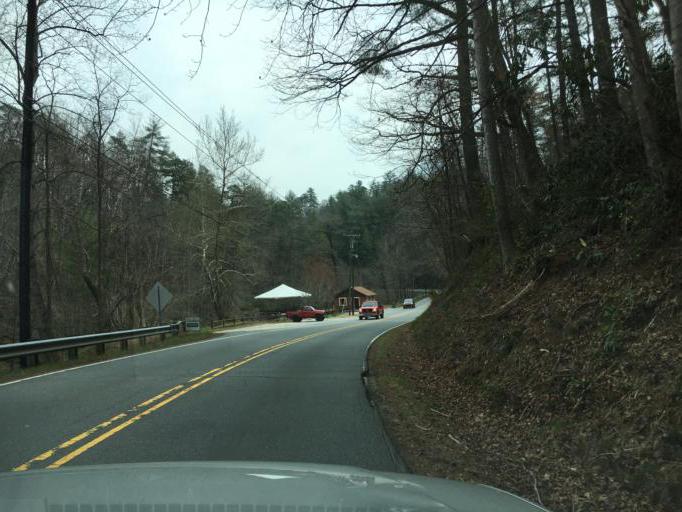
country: US
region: North Carolina
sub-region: Rutherford County
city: Lake Lure
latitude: 35.4219
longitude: -82.1728
